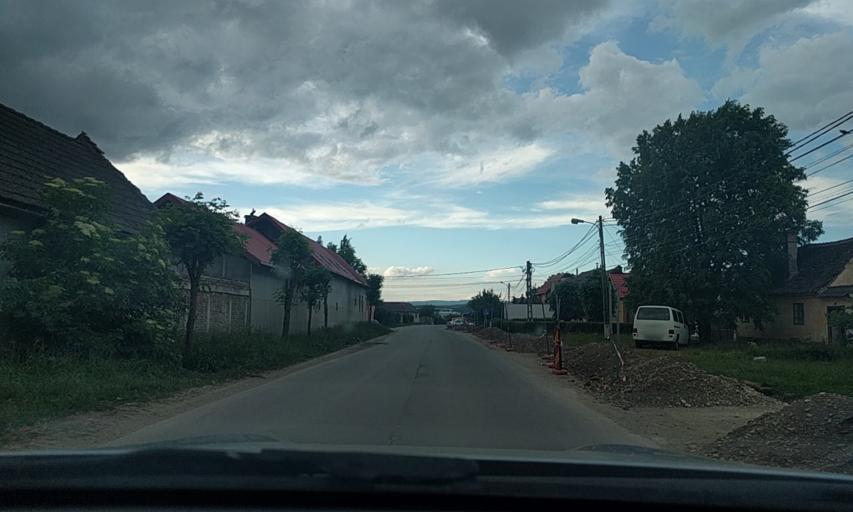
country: RO
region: Brasov
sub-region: Comuna Harman
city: Harman
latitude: 45.7165
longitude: 25.6945
